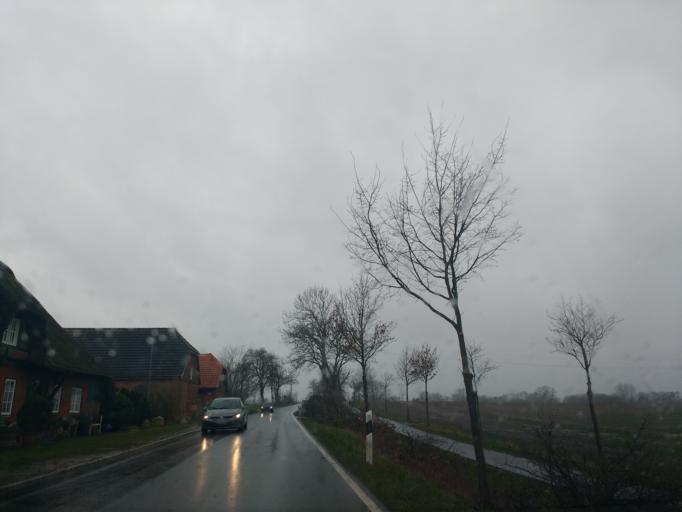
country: DE
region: Schleswig-Holstein
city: Gremersdorf
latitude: 54.3120
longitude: 10.9394
